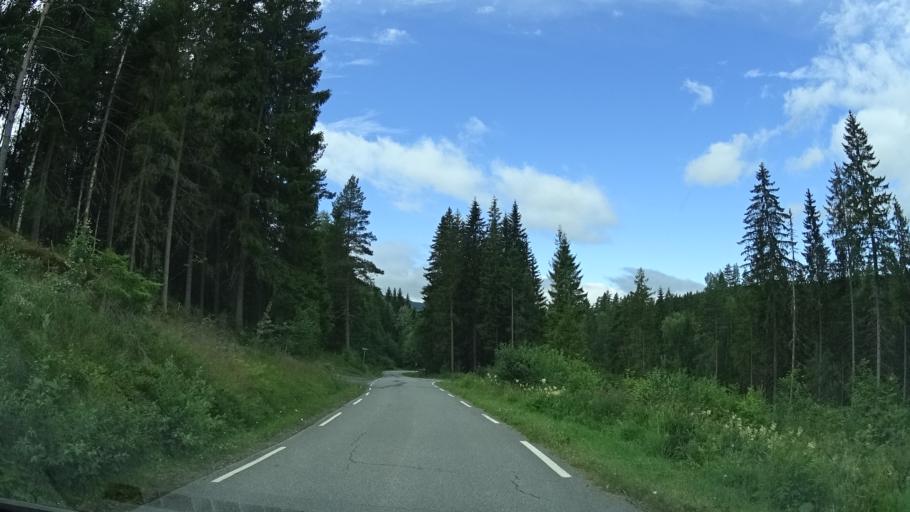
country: NO
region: Buskerud
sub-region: Ringerike
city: Honefoss
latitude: 60.2063
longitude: 10.0313
